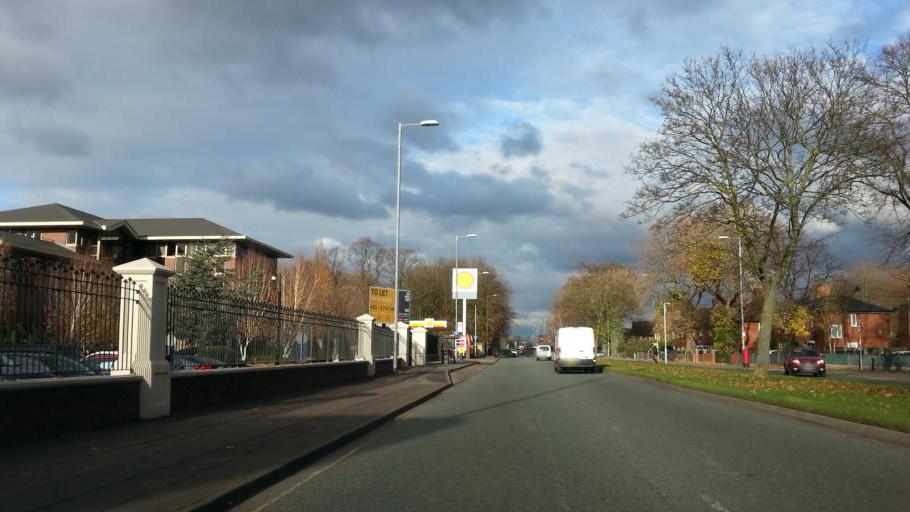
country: GB
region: England
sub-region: Manchester
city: Hulme
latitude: 53.4478
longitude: -2.2447
